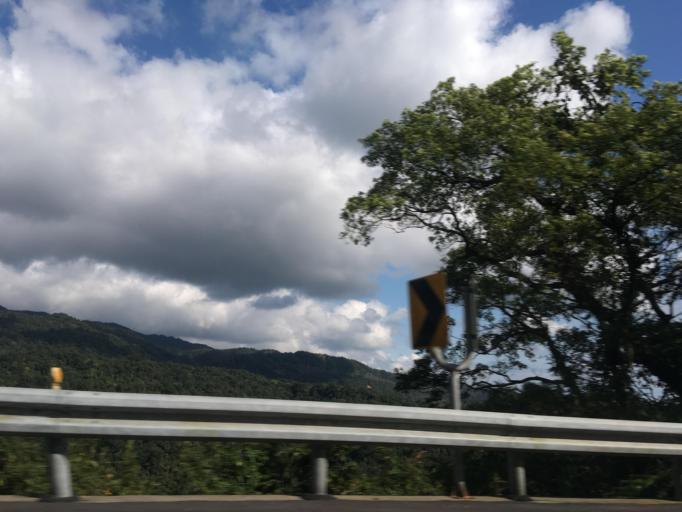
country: TW
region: Taiwan
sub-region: Yilan
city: Yilan
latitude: 24.7509
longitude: 121.6435
